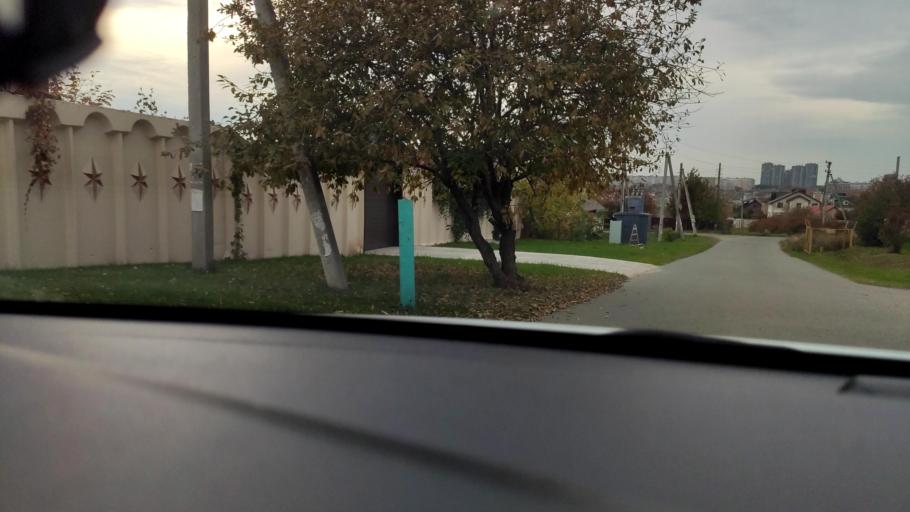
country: RU
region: Tatarstan
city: Stolbishchi
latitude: 55.7661
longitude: 49.2672
